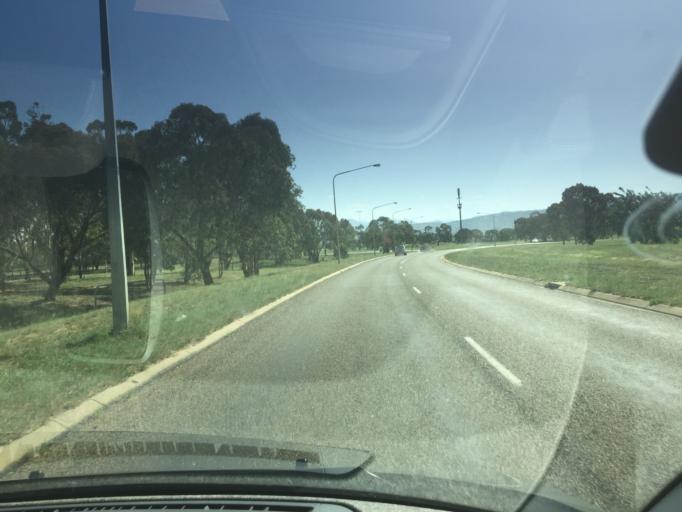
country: AU
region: Australian Capital Territory
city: Macarthur
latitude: -35.4227
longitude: 149.0924
